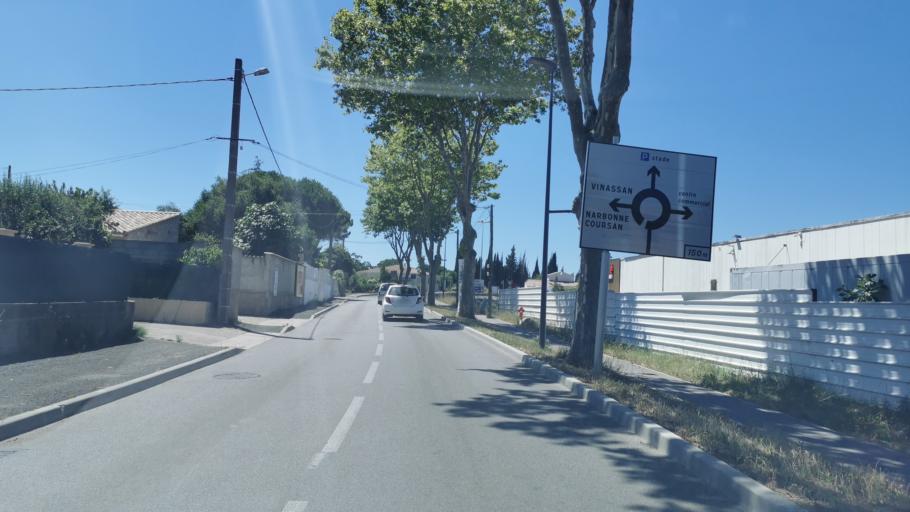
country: FR
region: Languedoc-Roussillon
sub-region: Departement de l'Aude
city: Fleury
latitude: 43.2384
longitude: 3.1131
